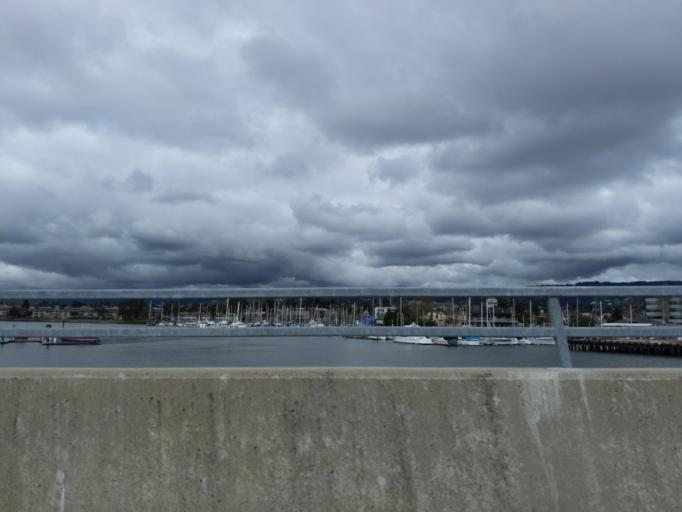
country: US
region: California
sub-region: Alameda County
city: Alameda
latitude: 37.7798
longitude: -122.2455
